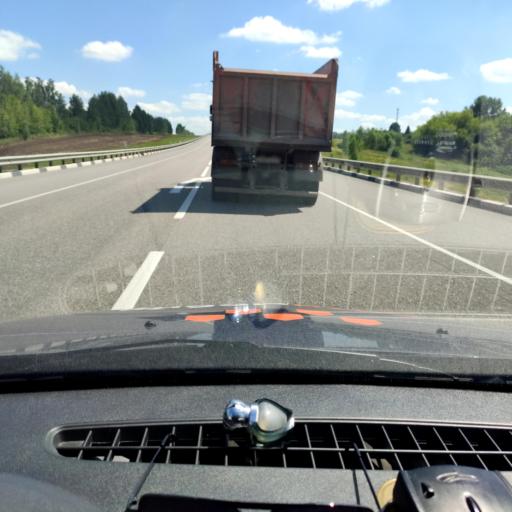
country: RU
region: Orjol
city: Zmiyevka
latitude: 52.8386
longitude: 36.2627
